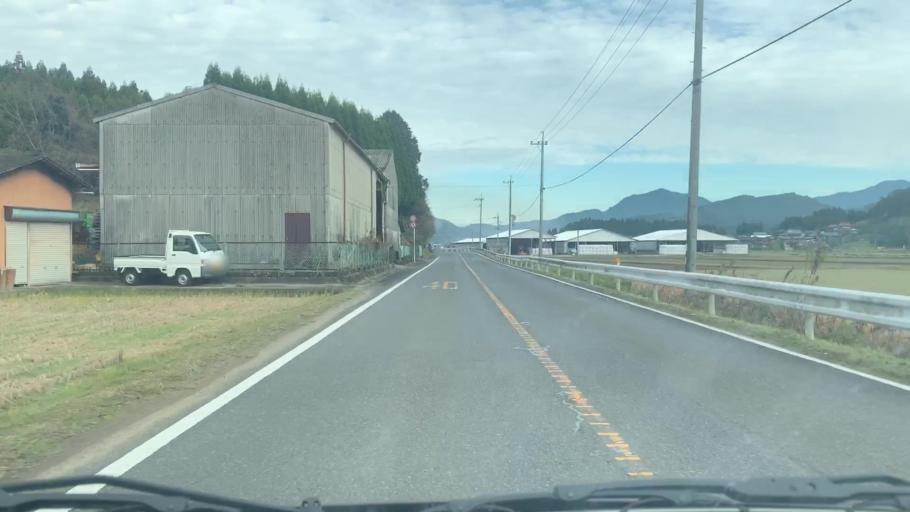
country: JP
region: Saga Prefecture
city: Takeocho-takeo
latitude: 33.2203
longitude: 129.9649
